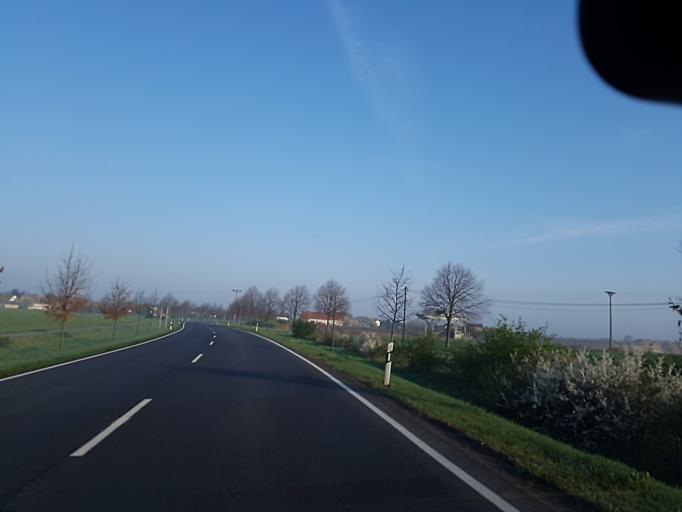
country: DE
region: Brandenburg
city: Muhlberg
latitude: 51.4427
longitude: 13.1806
